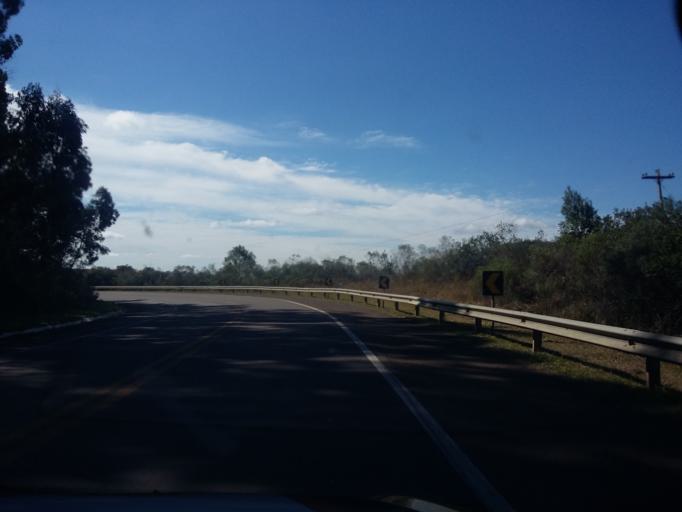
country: BR
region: Rio Grande do Sul
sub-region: Vacaria
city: Vacaria
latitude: -28.7008
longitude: -51.0759
